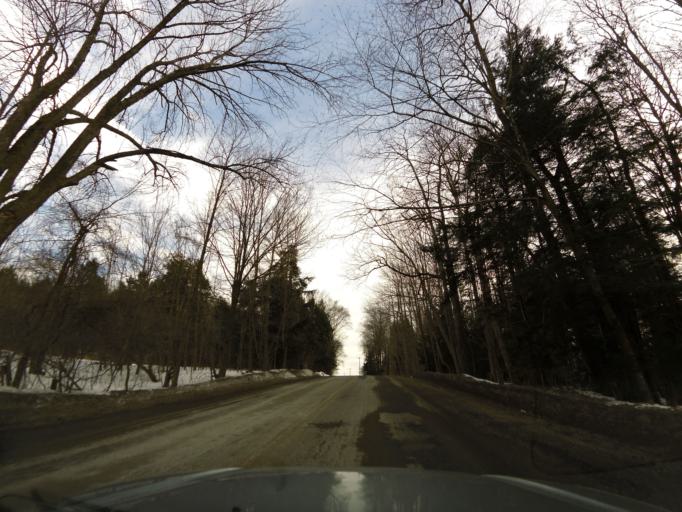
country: US
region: New York
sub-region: Cattaraugus County
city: Delevan
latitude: 42.4998
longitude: -78.5089
